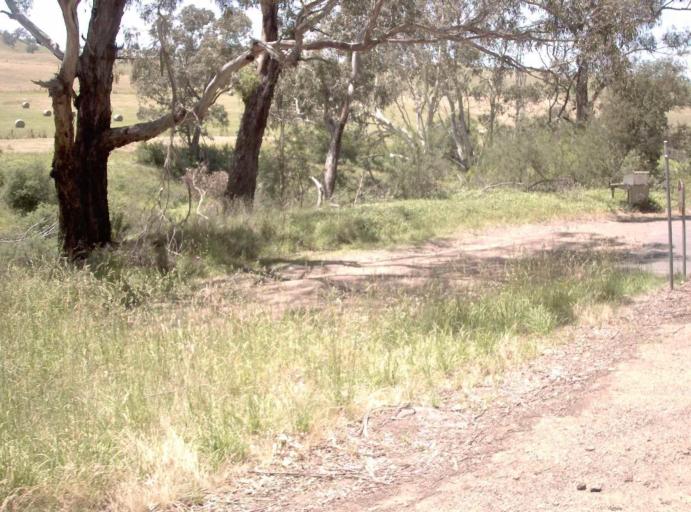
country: AU
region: Victoria
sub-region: East Gippsland
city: Bairnsdale
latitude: -37.3992
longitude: 147.8350
